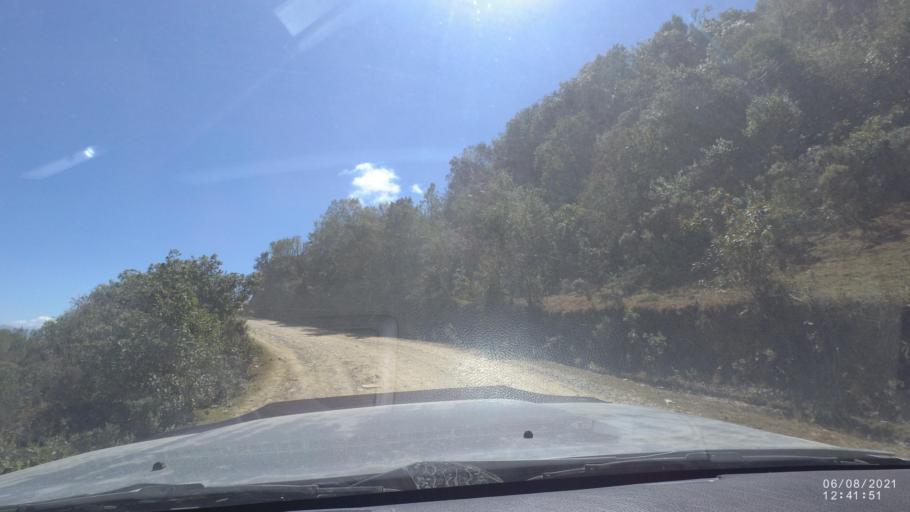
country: BO
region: Cochabamba
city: Colchani
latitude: -16.7806
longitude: -66.6658
